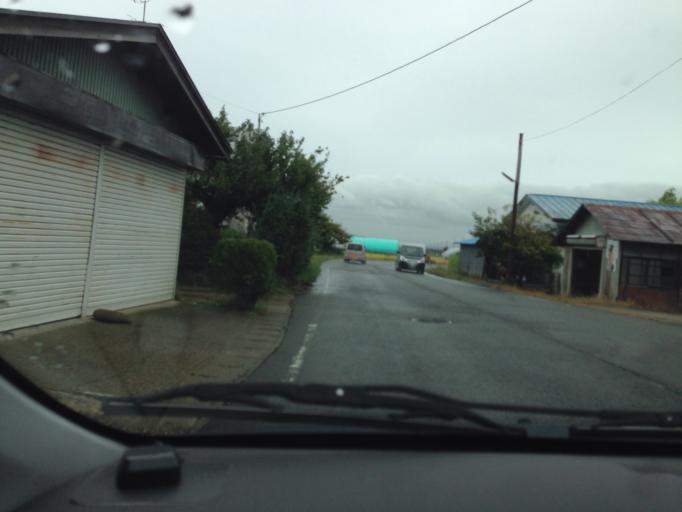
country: JP
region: Fukushima
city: Kitakata
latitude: 37.5246
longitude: 139.8192
